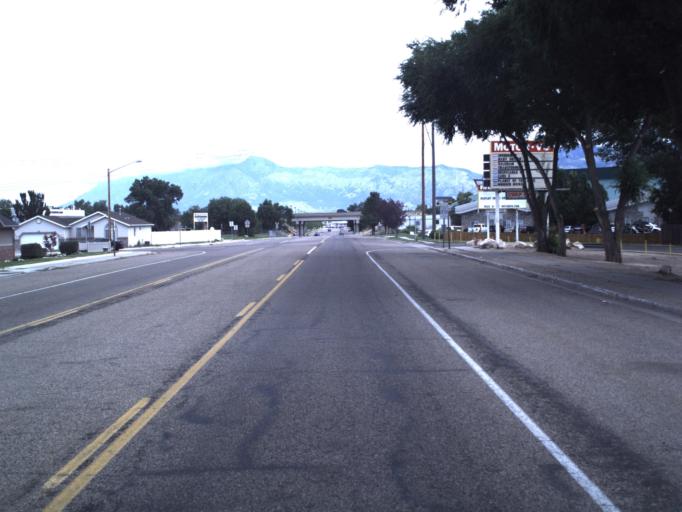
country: US
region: Utah
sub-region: Weber County
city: Riverdale
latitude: 41.1678
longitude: -112.0070
